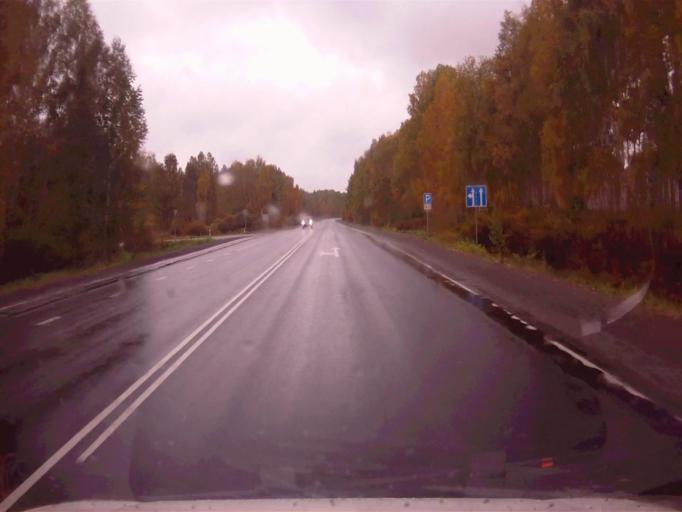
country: RU
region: Chelyabinsk
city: Argayash
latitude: 55.4784
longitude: 60.7731
